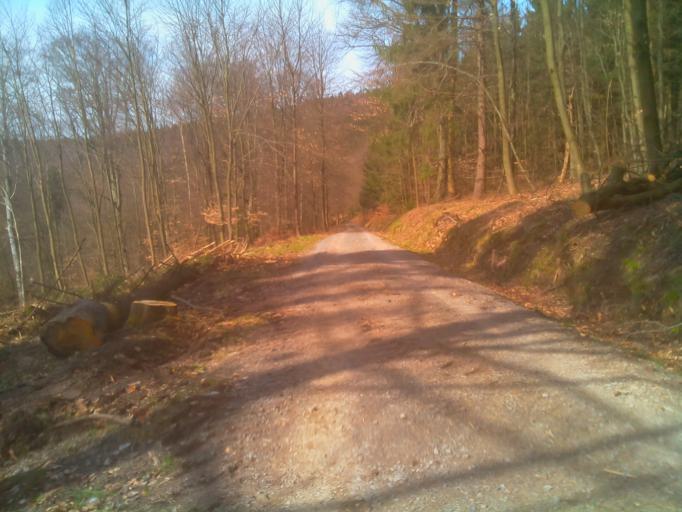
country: DE
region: Baden-Wuerttemberg
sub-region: Karlsruhe Region
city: Dossenheim
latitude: 49.4406
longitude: 8.7046
